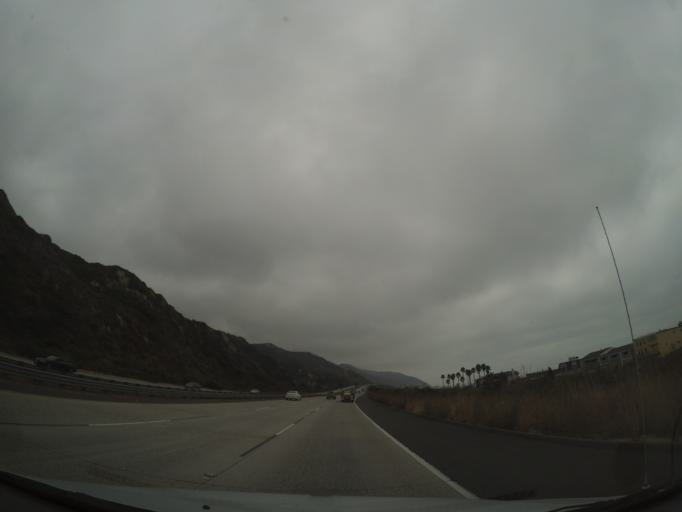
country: US
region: California
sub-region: Ventura County
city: Ventura
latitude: 34.3212
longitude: -119.3717
